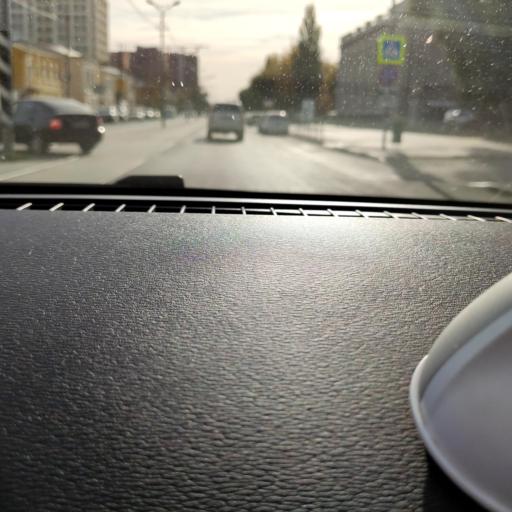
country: RU
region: Samara
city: Samara
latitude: 53.1953
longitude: 50.1041
